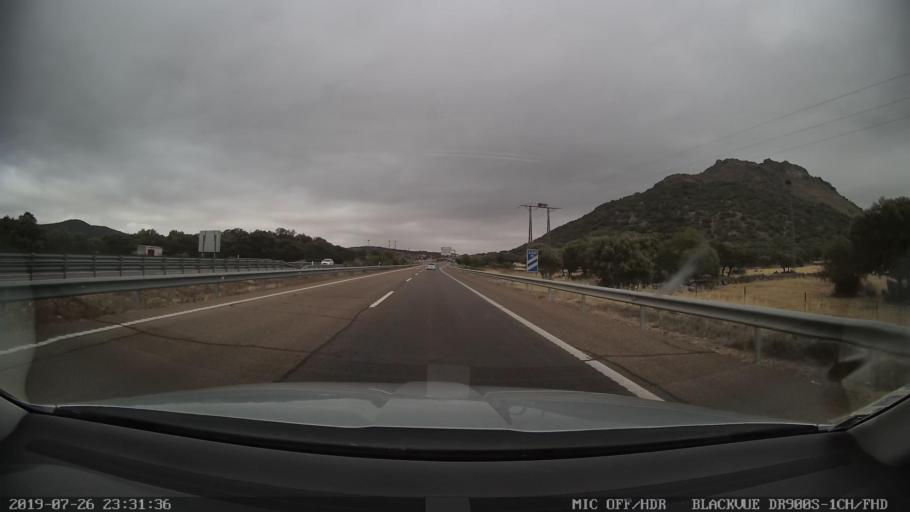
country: ES
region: Extremadura
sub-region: Provincia de Caceres
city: Puerto de Santa Cruz
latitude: 39.3020
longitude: -5.8567
